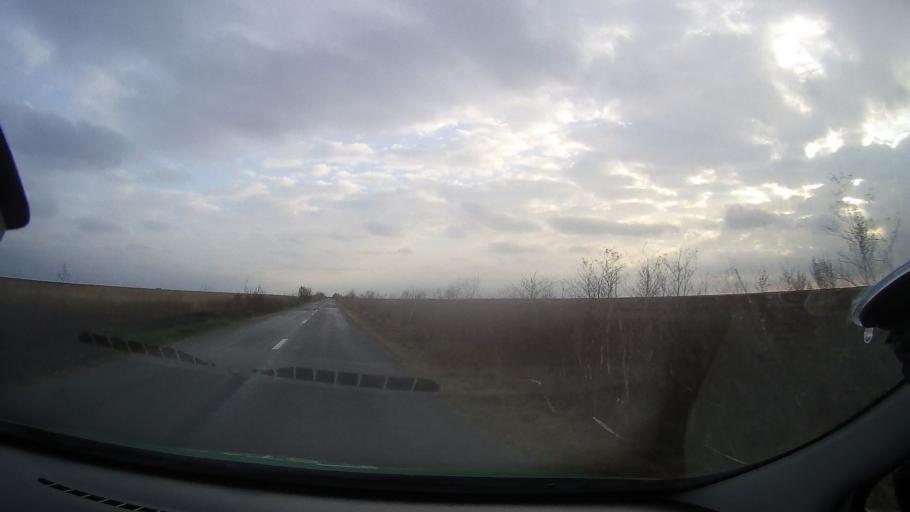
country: RO
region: Constanta
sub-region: Comuna Pestera
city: Pestera
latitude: 44.1392
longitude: 28.1176
